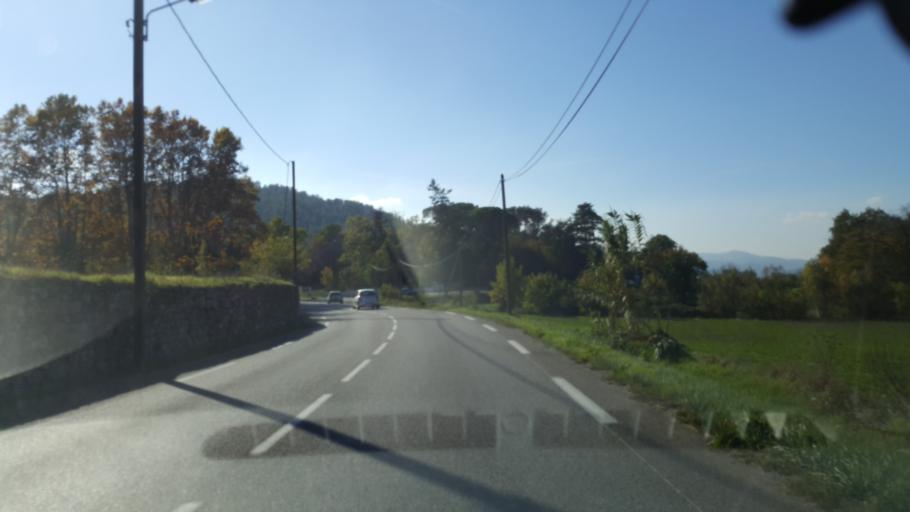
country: FR
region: Provence-Alpes-Cote d'Azur
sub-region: Departement du Var
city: Saint-Zacharie
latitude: 43.3794
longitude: 5.6986
